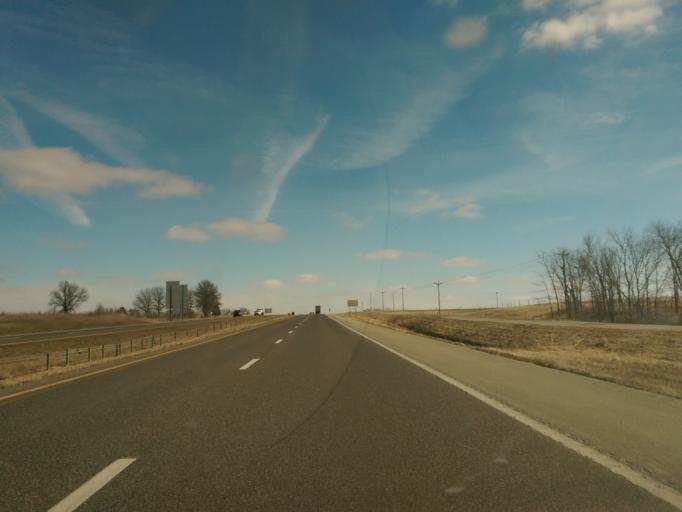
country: US
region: Missouri
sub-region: Callaway County
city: Fulton
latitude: 38.9440
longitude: -91.9237
